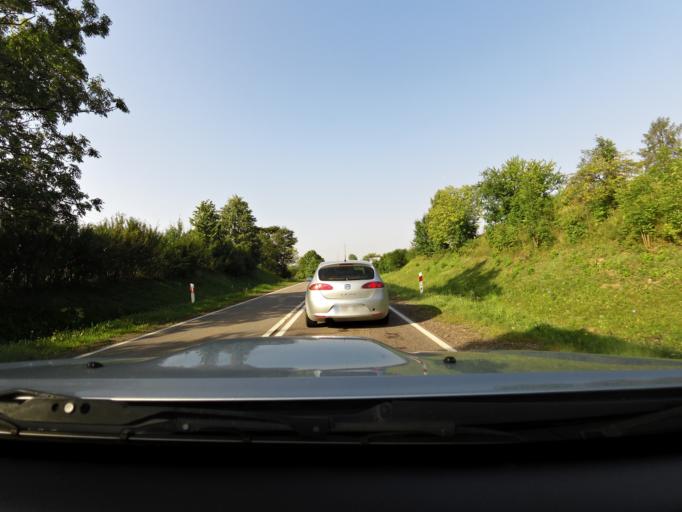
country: PL
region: Podlasie
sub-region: Powiat sejnenski
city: Sejny
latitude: 54.1109
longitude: 23.4196
